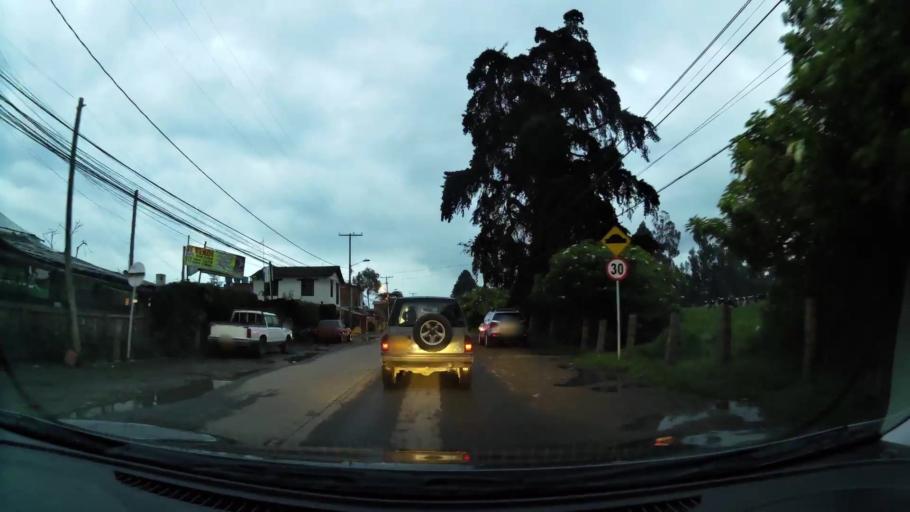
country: CO
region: Cundinamarca
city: Chia
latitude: 4.8372
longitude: -74.0697
